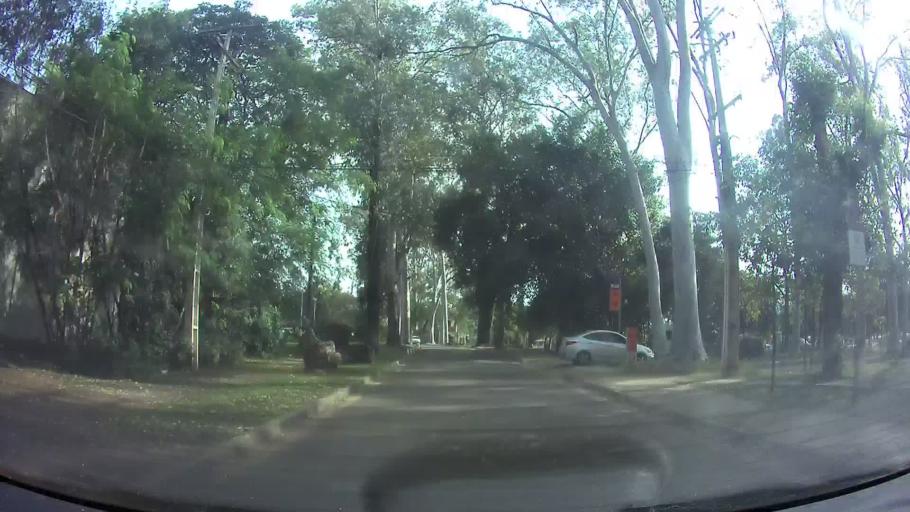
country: PY
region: Central
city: Fernando de la Mora
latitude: -25.3332
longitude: -57.5154
